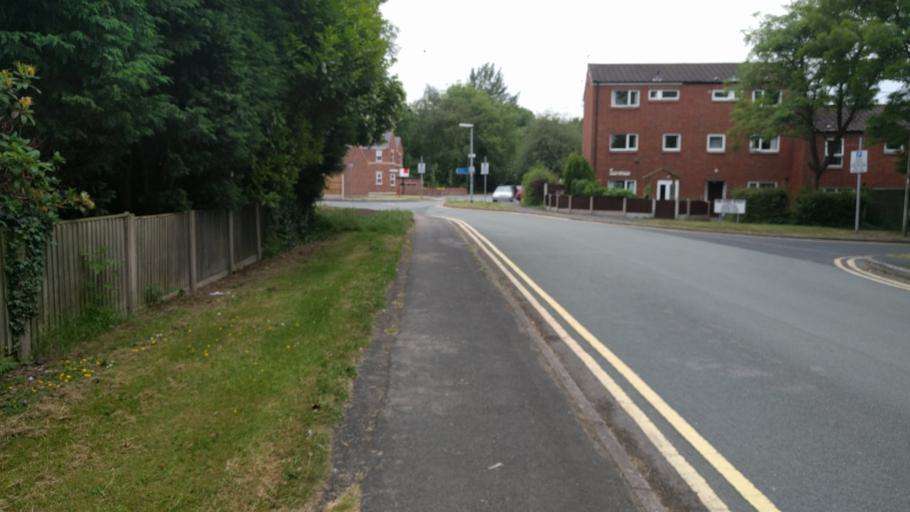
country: GB
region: England
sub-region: Warrington
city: Croft
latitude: 53.4231
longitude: -2.5277
